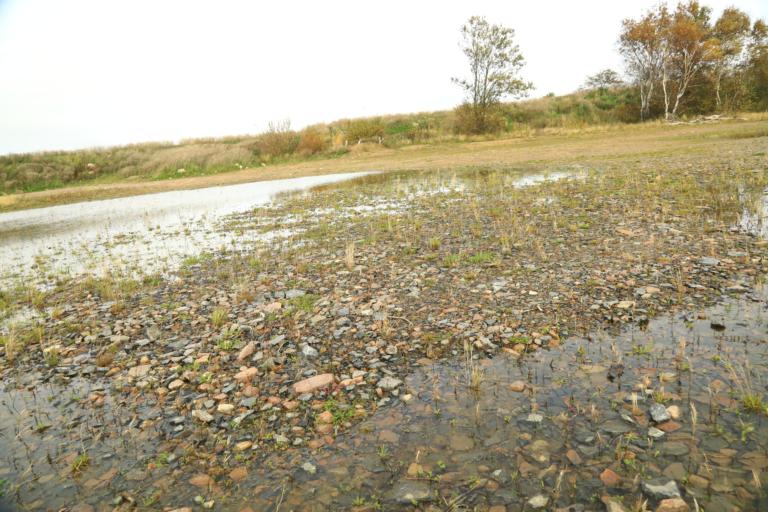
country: SE
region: Halland
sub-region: Varbergs Kommun
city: Varberg
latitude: 57.1218
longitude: 12.2393
